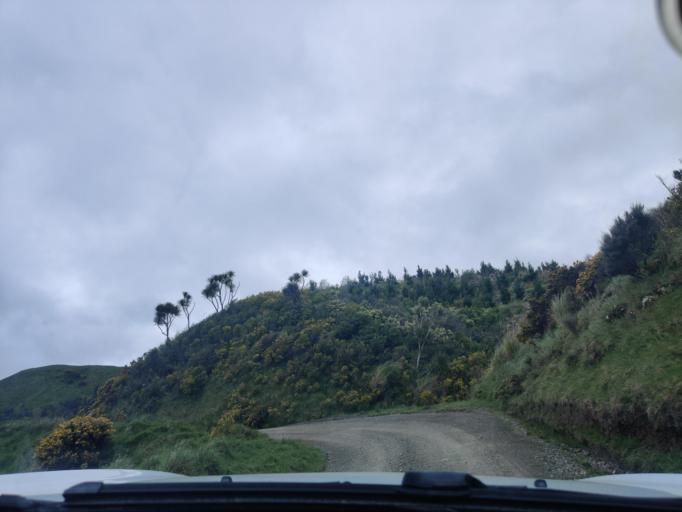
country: NZ
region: Manawatu-Wanganui
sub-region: Palmerston North City
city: Palmerston North
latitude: -40.2904
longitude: 175.8605
